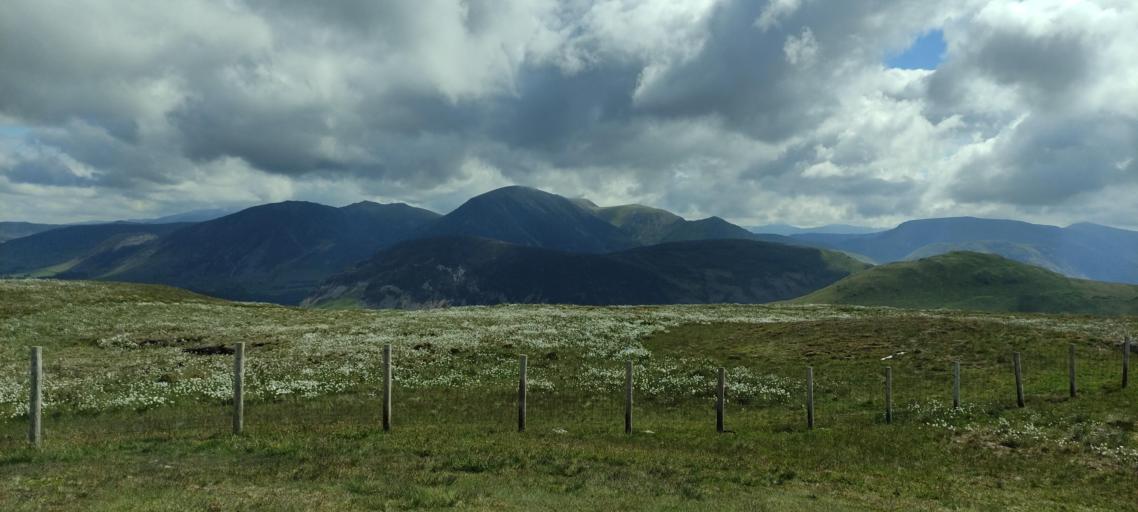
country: GB
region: England
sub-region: Cumbria
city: Cockermouth
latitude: 54.5530
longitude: -3.3668
